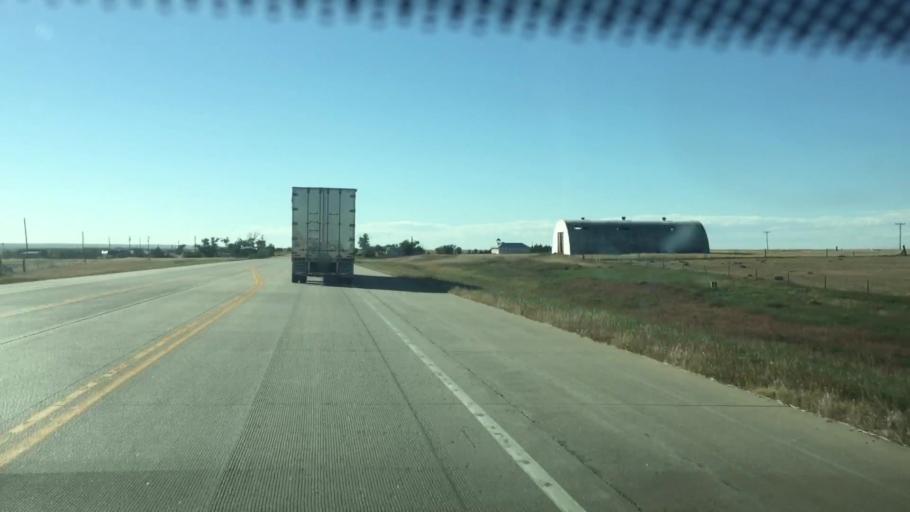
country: US
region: Colorado
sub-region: Kiowa County
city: Eads
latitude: 38.8255
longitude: -103.0004
